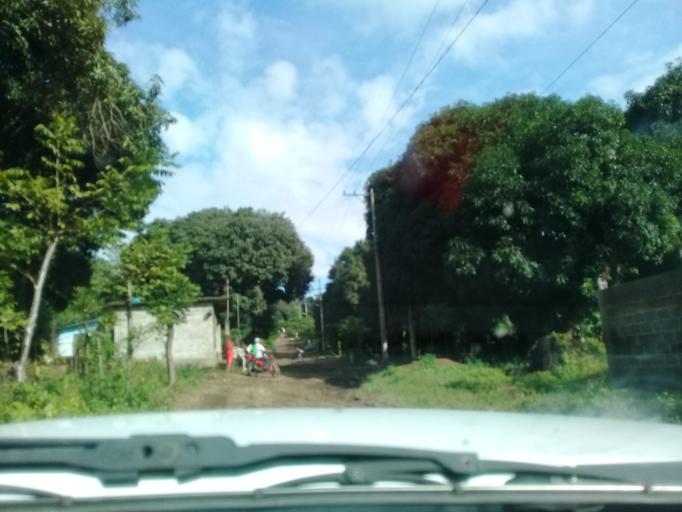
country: MX
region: Veracruz
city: Catemaco
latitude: 18.4346
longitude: -95.1311
